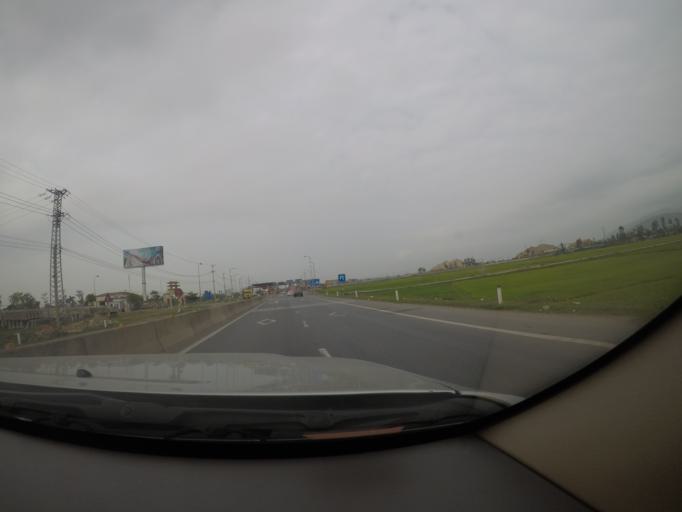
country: VN
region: Quang Binh
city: Ba Don
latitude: 17.8915
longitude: 106.4524
